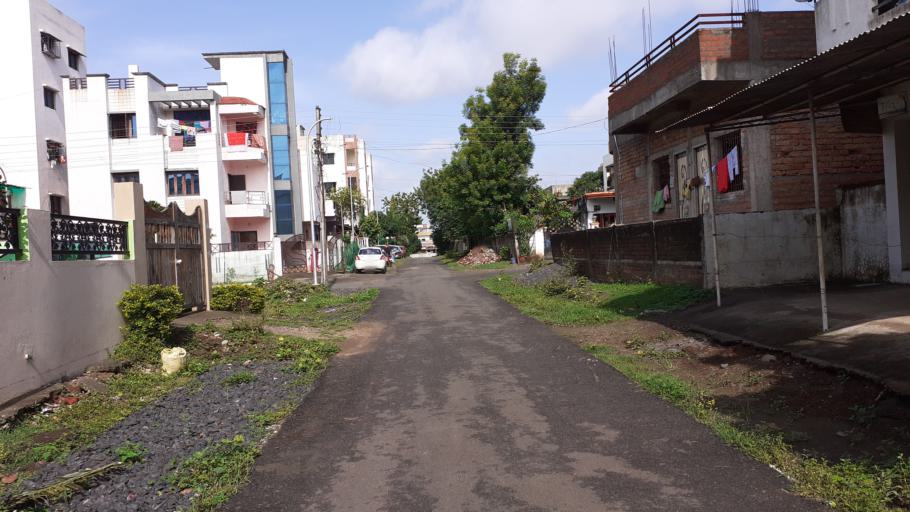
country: IN
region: Maharashtra
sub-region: Nagpur Division
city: Nagpur
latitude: 21.0974
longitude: 79.1107
